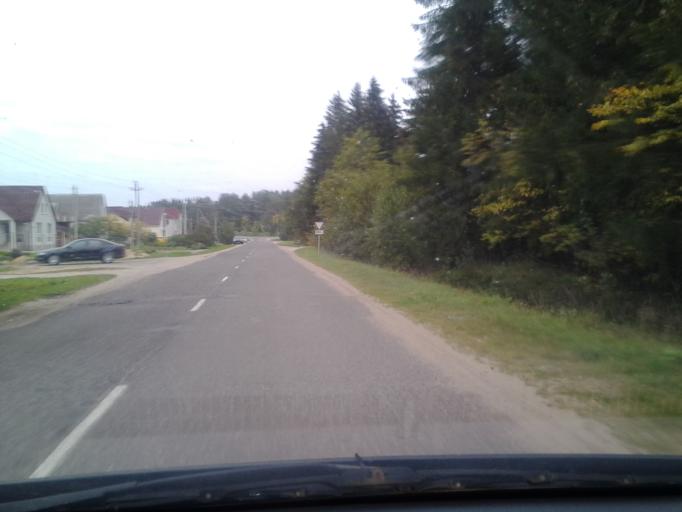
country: BY
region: Vitebsk
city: Pastavy
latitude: 55.0929
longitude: 26.8405
